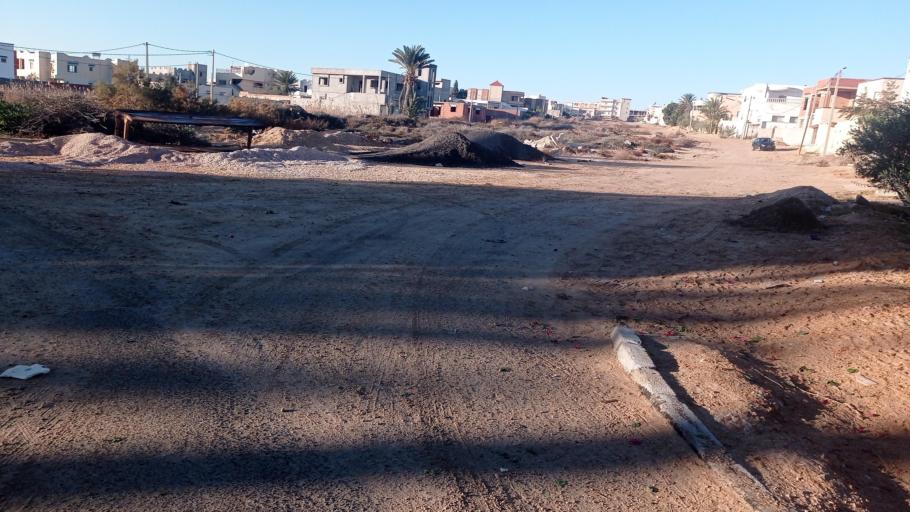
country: TN
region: Qabis
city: Gabes
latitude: 33.8496
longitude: 10.1181
